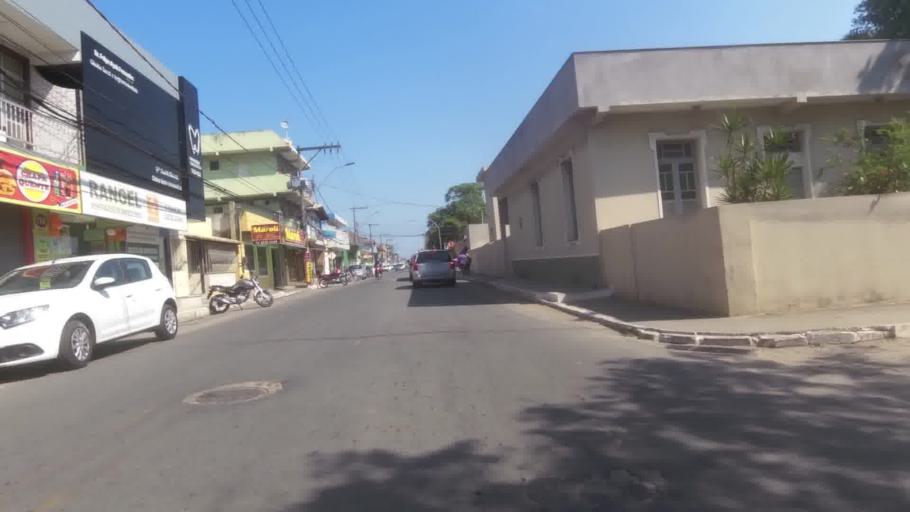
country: BR
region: Espirito Santo
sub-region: Itapemirim
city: Itapemirim
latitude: -21.0102
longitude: -40.8095
